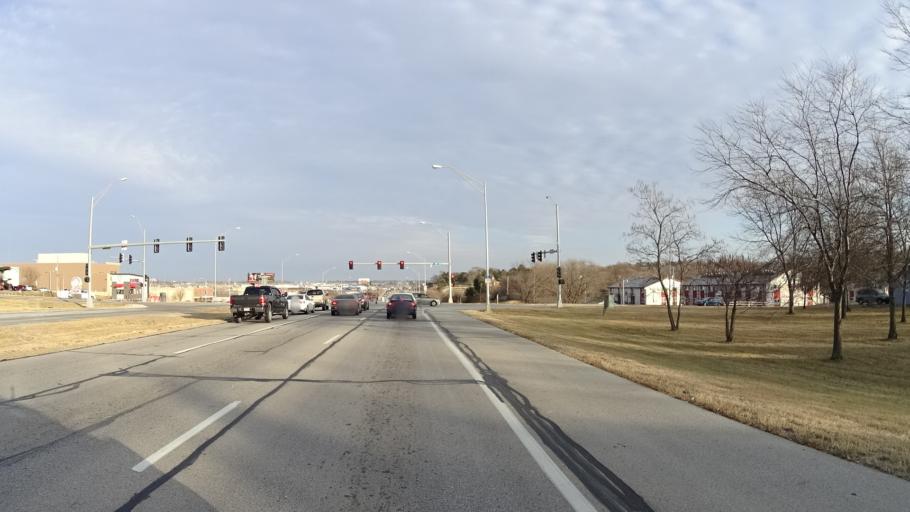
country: US
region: Nebraska
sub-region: Douglas County
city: Ralston
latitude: 41.2124
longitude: -96.0534
